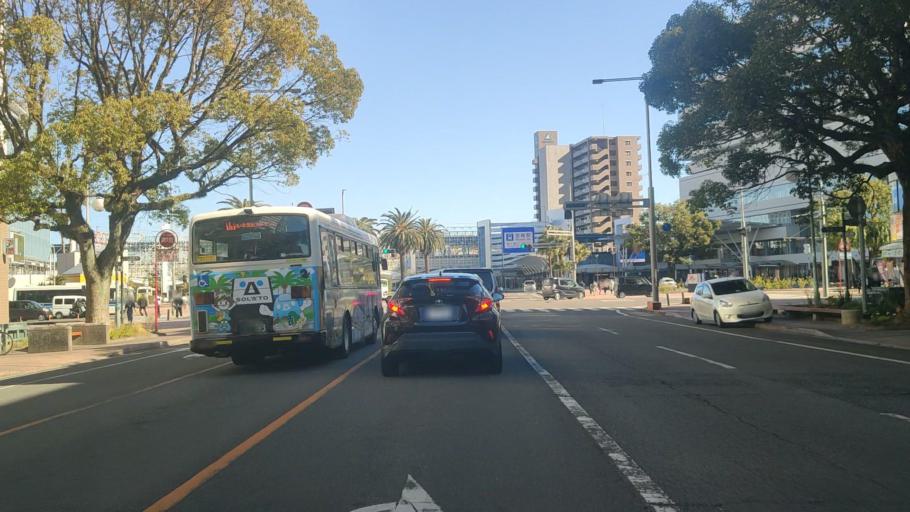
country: JP
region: Miyazaki
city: Miyazaki-shi
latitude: 31.9157
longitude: 131.4297
